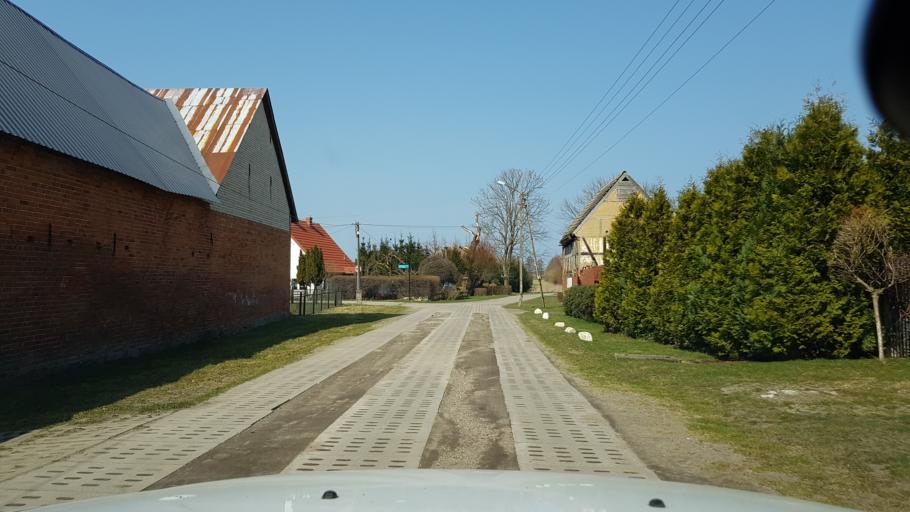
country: PL
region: West Pomeranian Voivodeship
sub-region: Powiat slawienski
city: Darlowo
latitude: 54.4612
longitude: 16.4329
